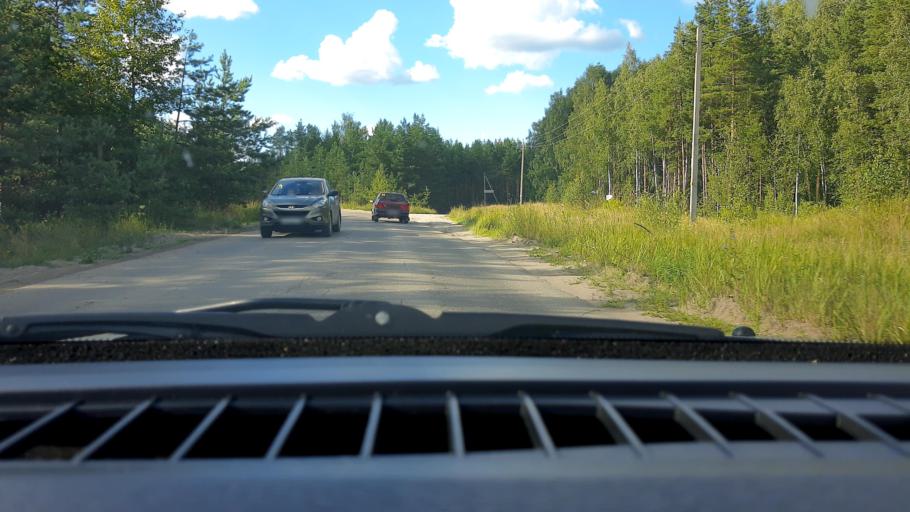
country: RU
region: Nizjnij Novgorod
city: Babino
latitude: 56.3074
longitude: 43.6324
